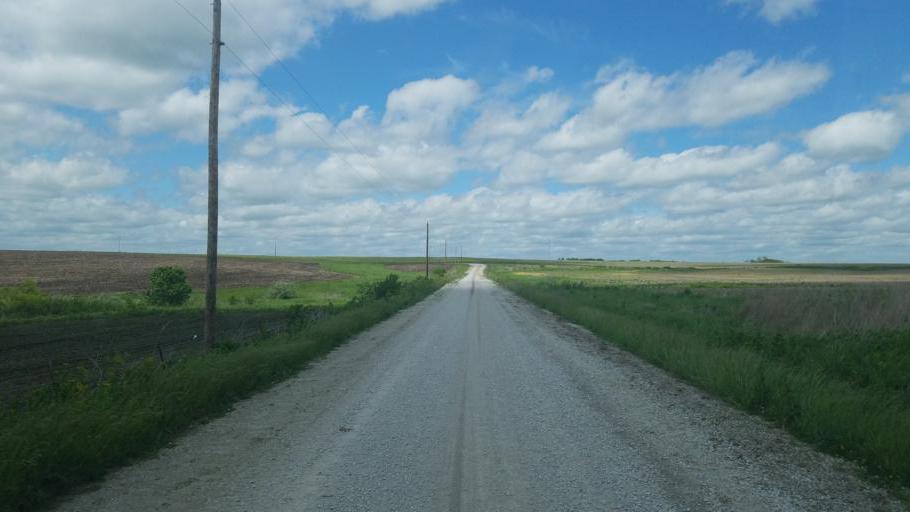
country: US
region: Iowa
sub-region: Decatur County
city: Lamoni
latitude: 40.4976
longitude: -93.9842
